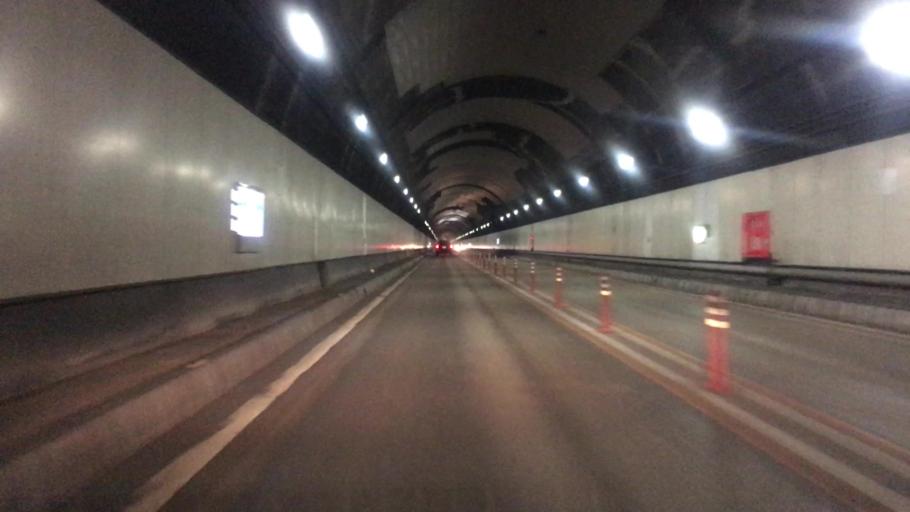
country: JP
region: Kyoto
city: Fukuchiyama
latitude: 35.2975
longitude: 134.9497
